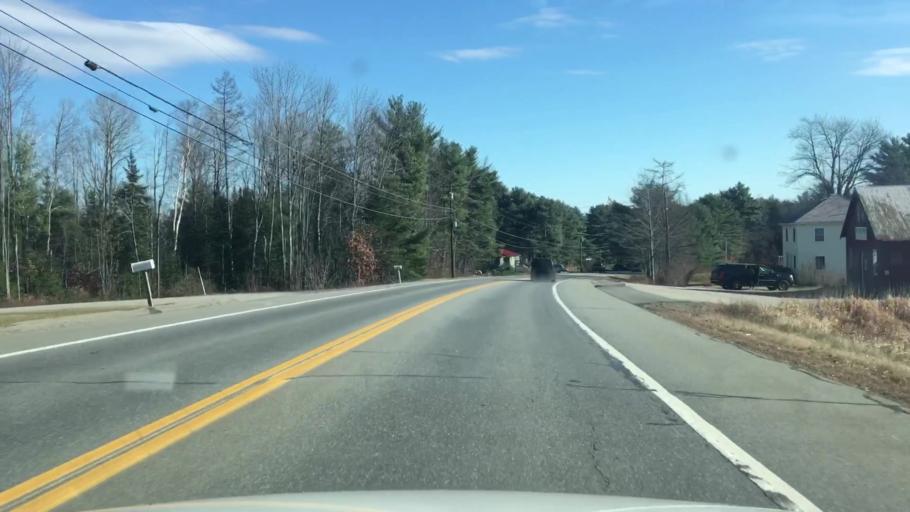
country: US
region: Maine
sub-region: Kennebec County
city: Windsor
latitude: 44.2689
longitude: -69.5698
